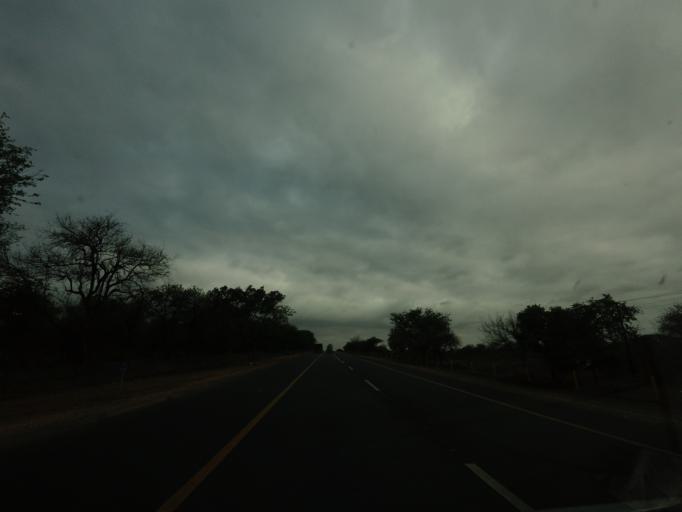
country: ZA
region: Mpumalanga
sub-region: Ehlanzeni District
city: Komatipoort
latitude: -25.4410
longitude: 31.7196
